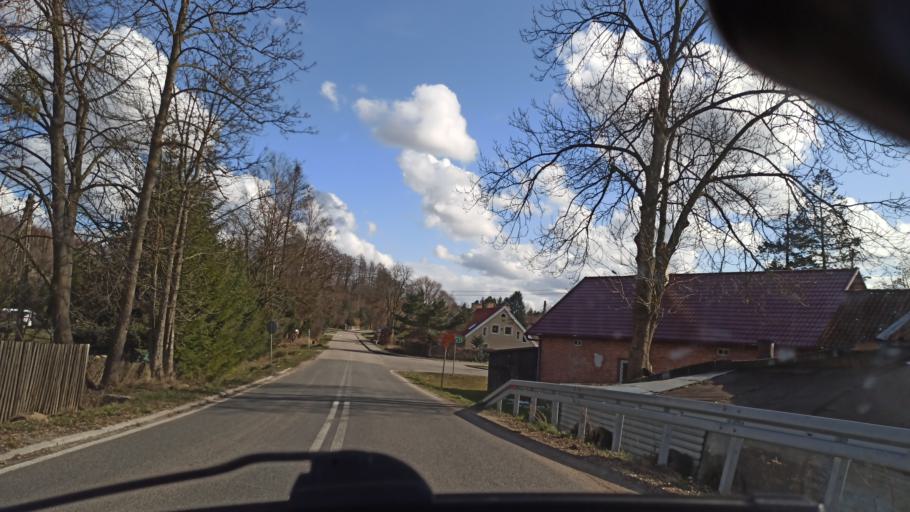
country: PL
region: Warmian-Masurian Voivodeship
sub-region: Powiat elblaski
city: Tolkmicko
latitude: 54.2688
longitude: 19.4745
